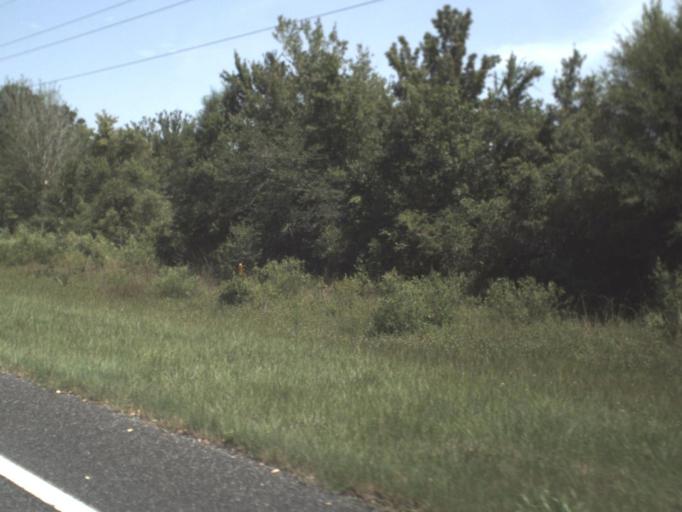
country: US
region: Florida
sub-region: Taylor County
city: Steinhatchee
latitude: 29.6838
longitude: -83.2642
